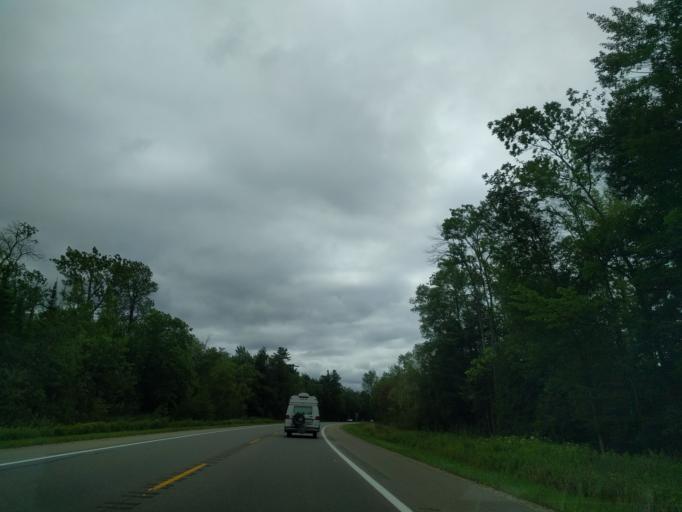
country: US
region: Michigan
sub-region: Menominee County
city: Menominee
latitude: 45.2975
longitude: -87.4398
